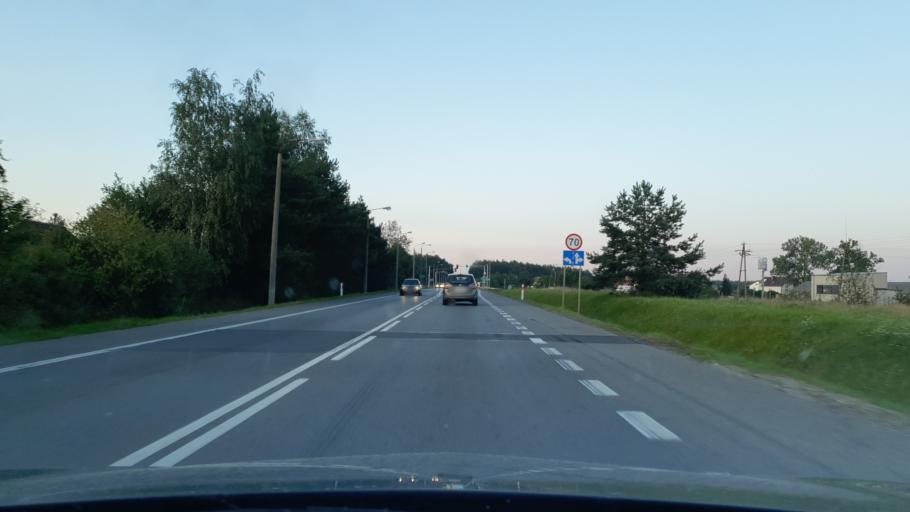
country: PL
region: Pomeranian Voivodeship
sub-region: Powiat leborski
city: Lebork
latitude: 54.5440
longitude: 17.7869
